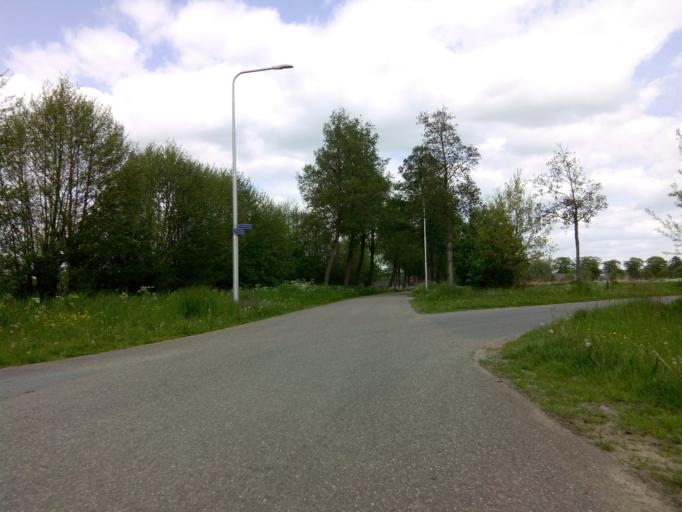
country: NL
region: Gelderland
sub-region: Gemeente Ede
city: Lunteren
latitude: 52.0608
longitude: 5.6304
